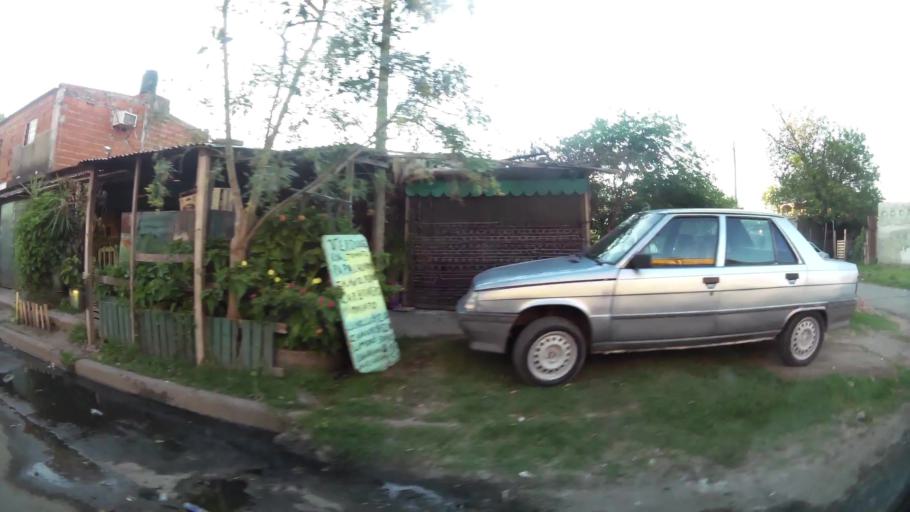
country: AR
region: Santa Fe
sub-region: Departamento de Rosario
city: Rosario
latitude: -32.9623
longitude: -60.6808
